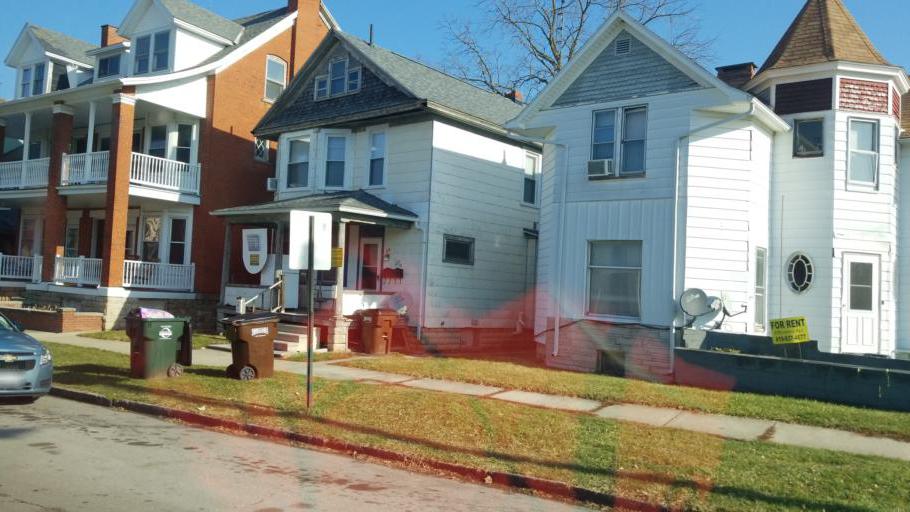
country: US
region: Ohio
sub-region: Seneca County
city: Tiffin
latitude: 41.1087
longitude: -83.1773
